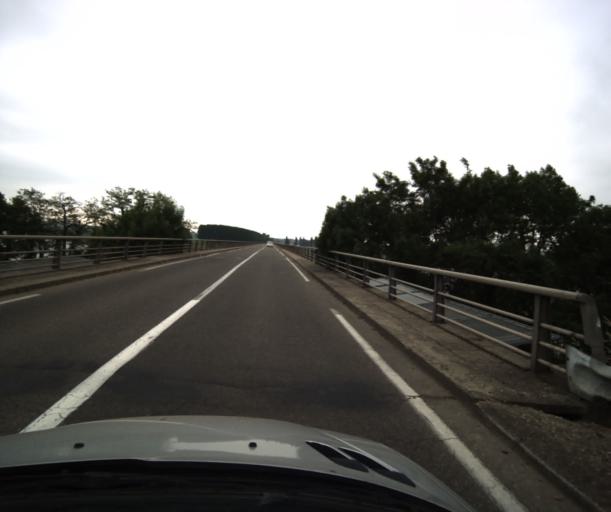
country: FR
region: Midi-Pyrenees
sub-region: Departement du Tarn-et-Garonne
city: Saint-Nicolas-de-la-Grave
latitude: 44.0856
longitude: 0.9852
